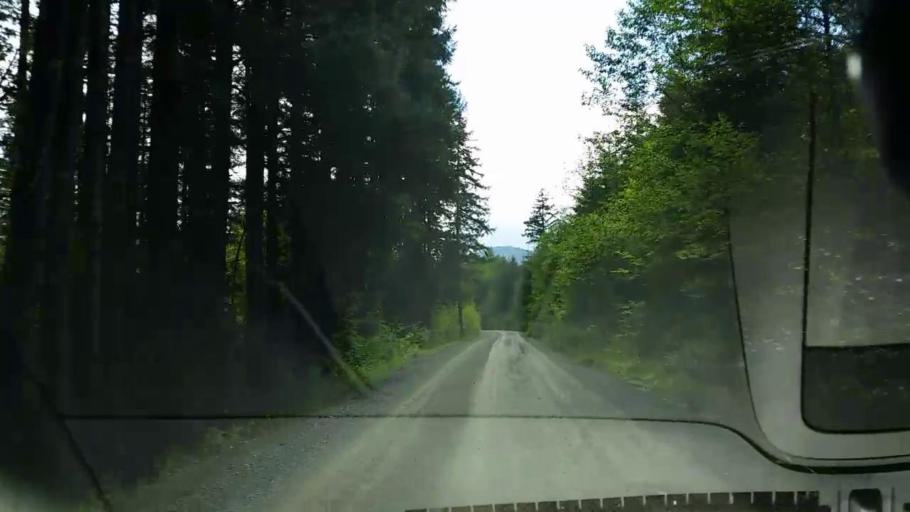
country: US
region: Washington
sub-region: Mason County
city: Shelton
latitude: 47.3556
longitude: -123.2879
